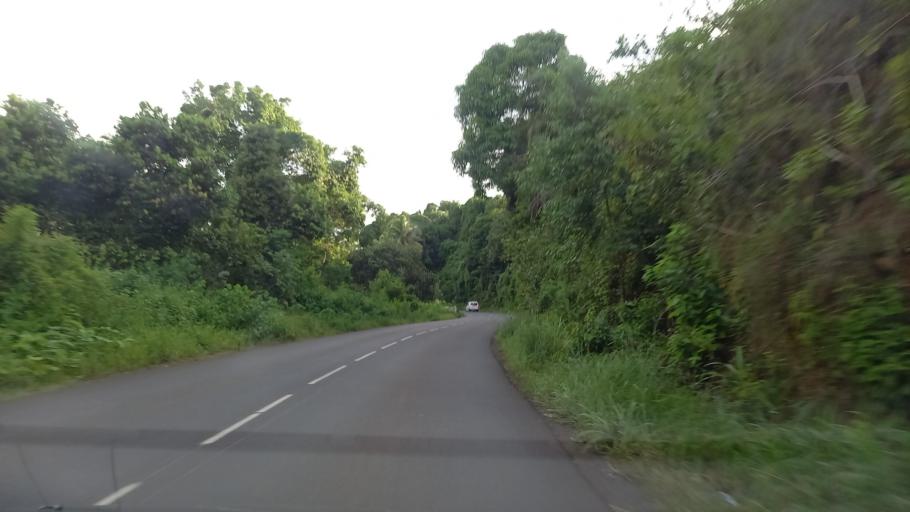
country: YT
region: M'Tsangamouji
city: M'Tsangamouji
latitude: -12.7543
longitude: 45.1122
